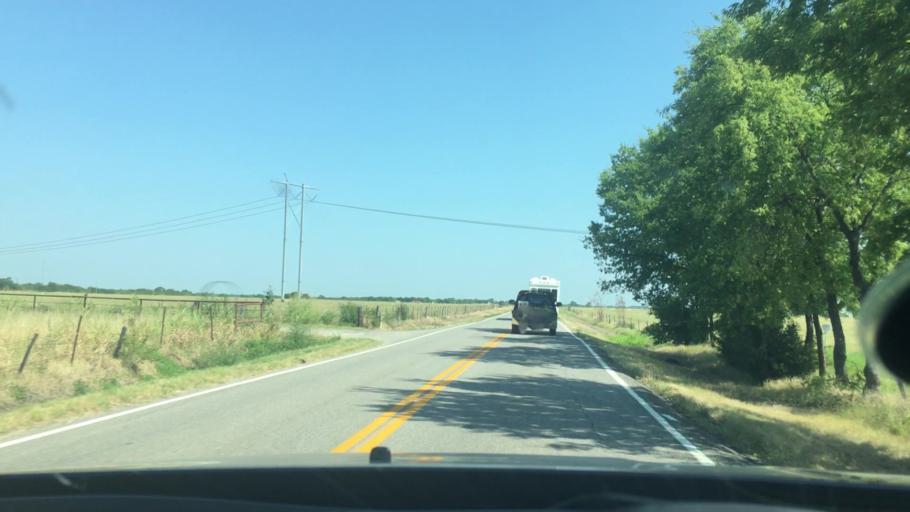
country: US
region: Oklahoma
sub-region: Johnston County
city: Tishomingo
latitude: 34.1647
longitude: -96.5086
